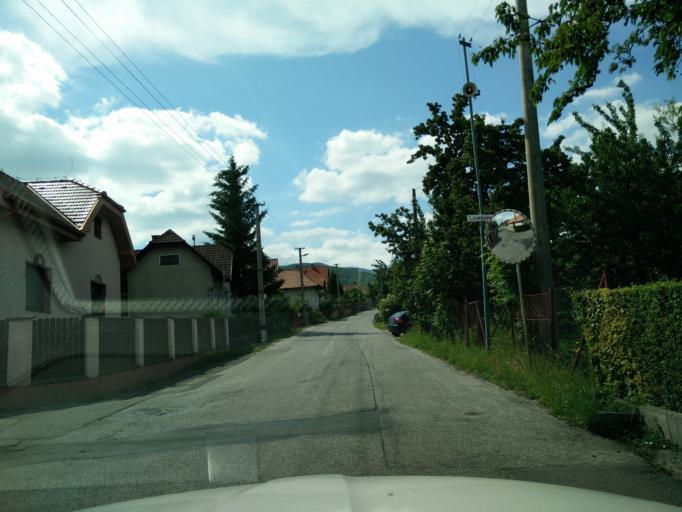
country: SK
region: Nitriansky
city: Bojnice
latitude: 48.8275
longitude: 18.6004
